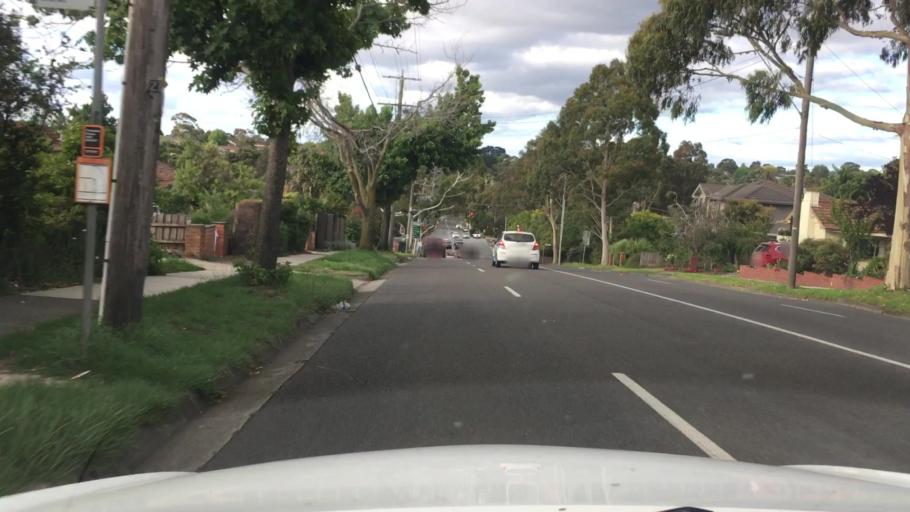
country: AU
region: Victoria
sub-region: Whitehorse
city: Burwood
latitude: -37.8721
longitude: 145.1296
